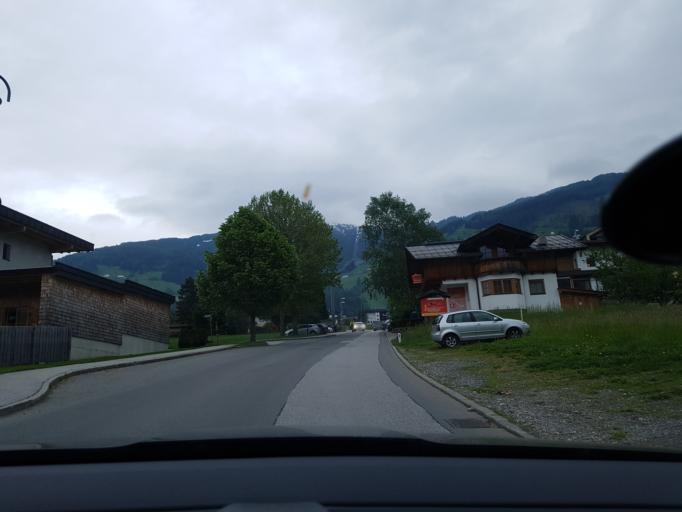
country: AT
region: Tyrol
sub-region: Politischer Bezirk Schwaz
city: Fugen
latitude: 47.3394
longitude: 11.8490
